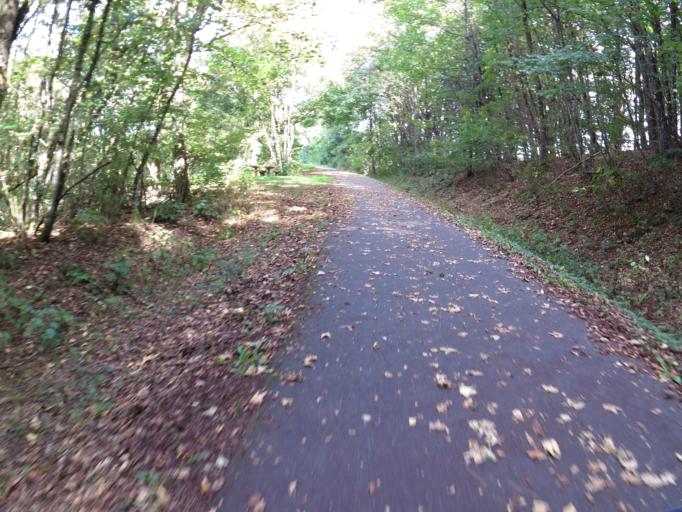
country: DE
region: Rheinland-Pfalz
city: Arzfeld
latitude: 50.0876
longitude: 6.2790
